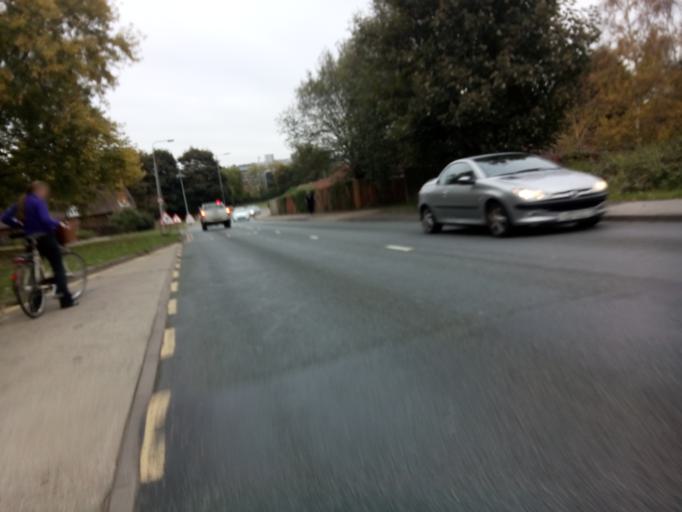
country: GB
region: England
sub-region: Suffolk
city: Ipswich
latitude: 52.0495
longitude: 1.1378
